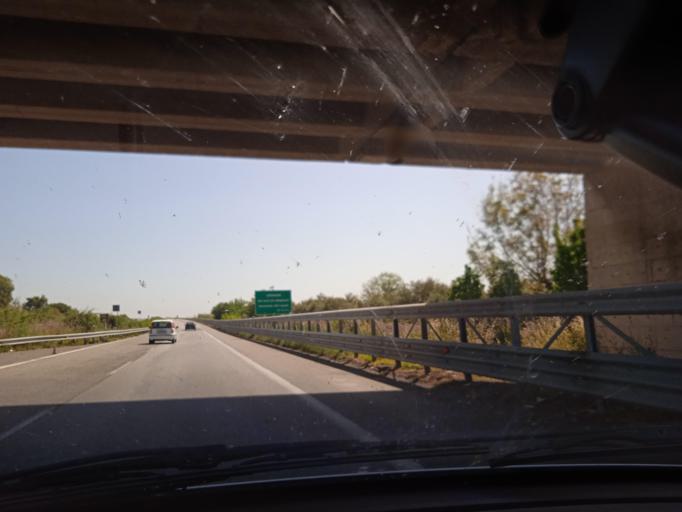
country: IT
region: Sicily
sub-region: Messina
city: Barcellona Pozzo di Gotto
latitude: 38.1595
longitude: 15.1944
